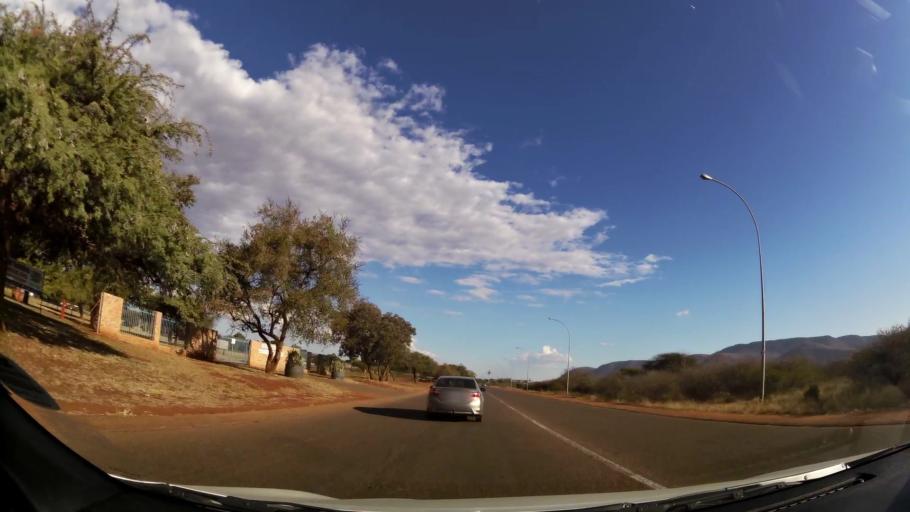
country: ZA
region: Limpopo
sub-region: Waterberg District Municipality
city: Mokopane
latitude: -24.1959
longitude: 29.0039
